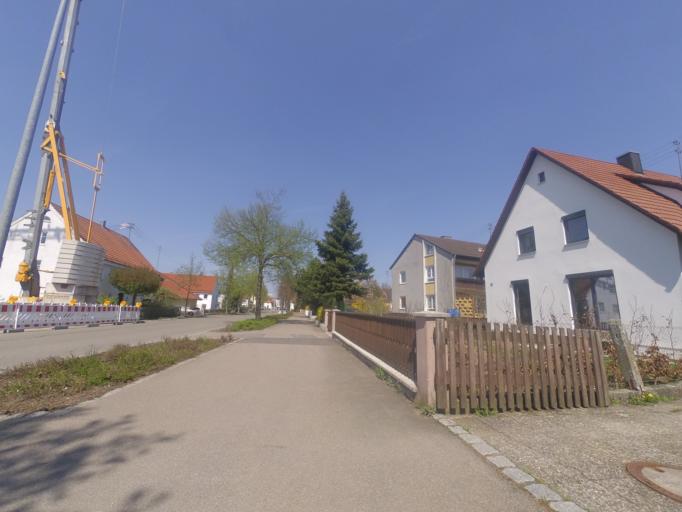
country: DE
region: Bavaria
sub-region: Swabia
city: Weissenhorn
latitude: 48.2950
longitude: 10.1608
